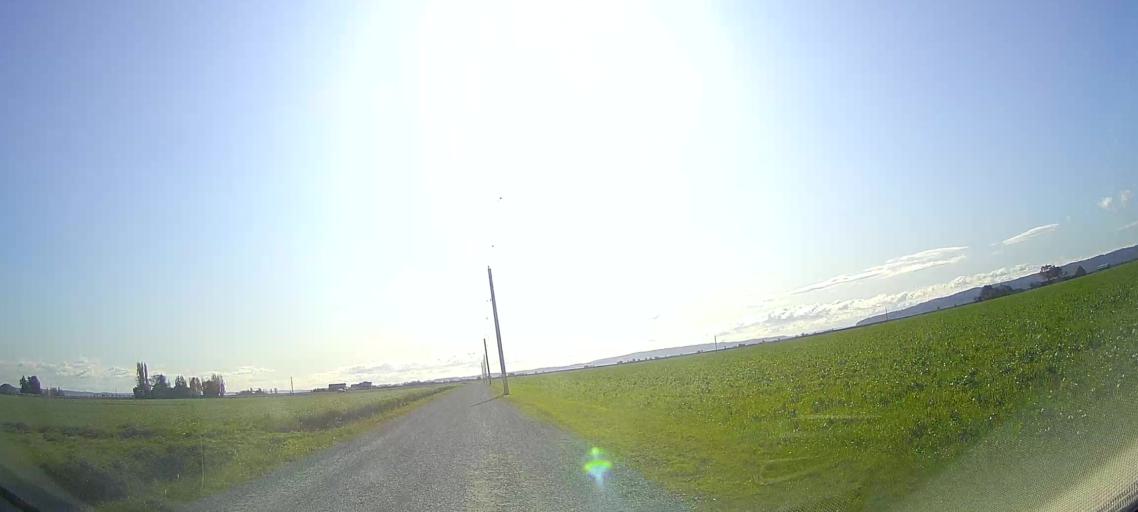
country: US
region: Washington
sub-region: Skagit County
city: Mount Vernon
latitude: 48.3590
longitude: -122.4496
